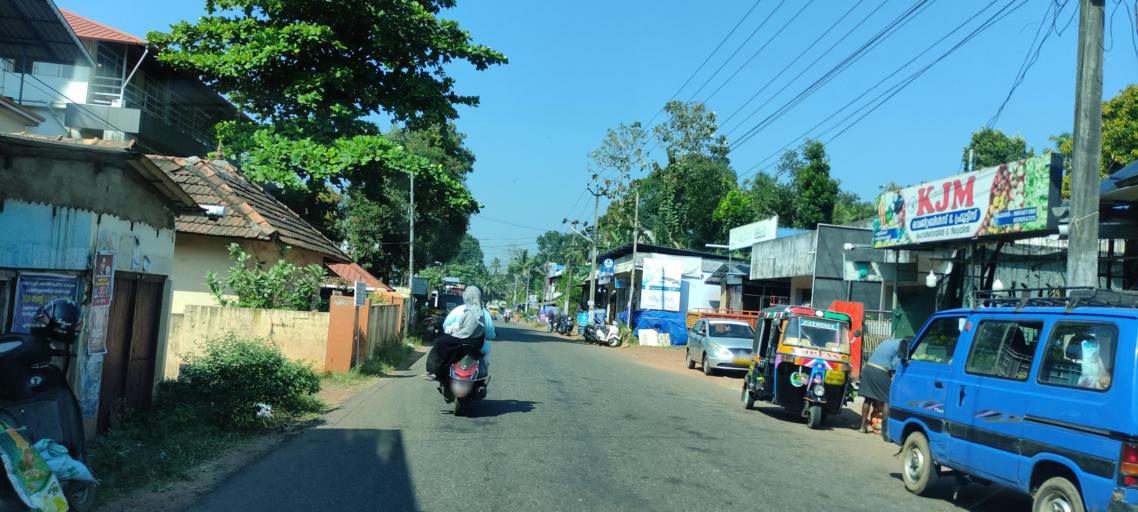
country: IN
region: Kerala
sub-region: Kollam
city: Panmana
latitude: 9.0419
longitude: 76.5897
